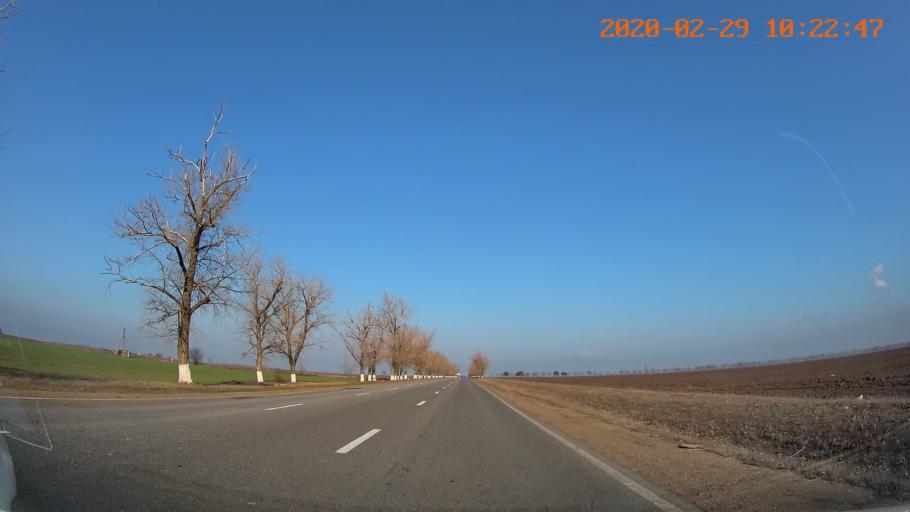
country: MD
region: Telenesti
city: Tiraspolul Nou
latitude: 46.8793
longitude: 29.6053
